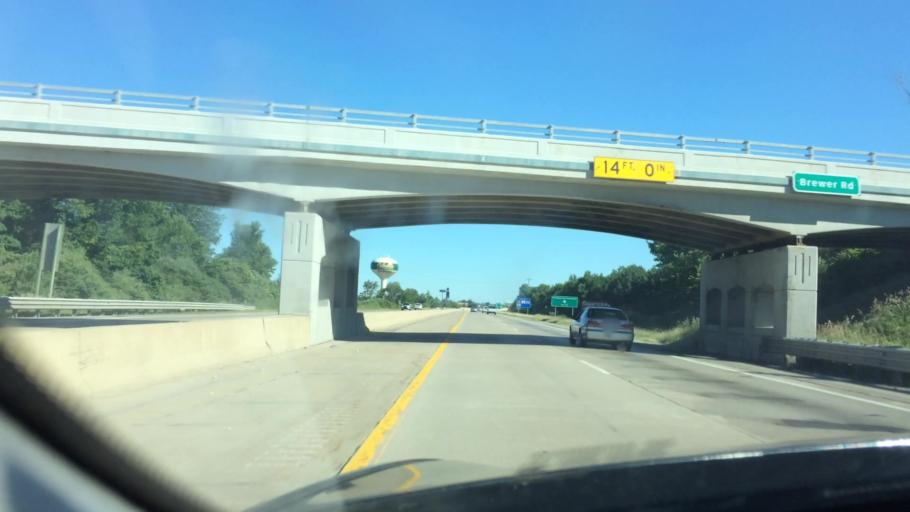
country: US
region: Michigan
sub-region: Monroe County
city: Dundee
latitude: 41.9499
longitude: -83.6684
